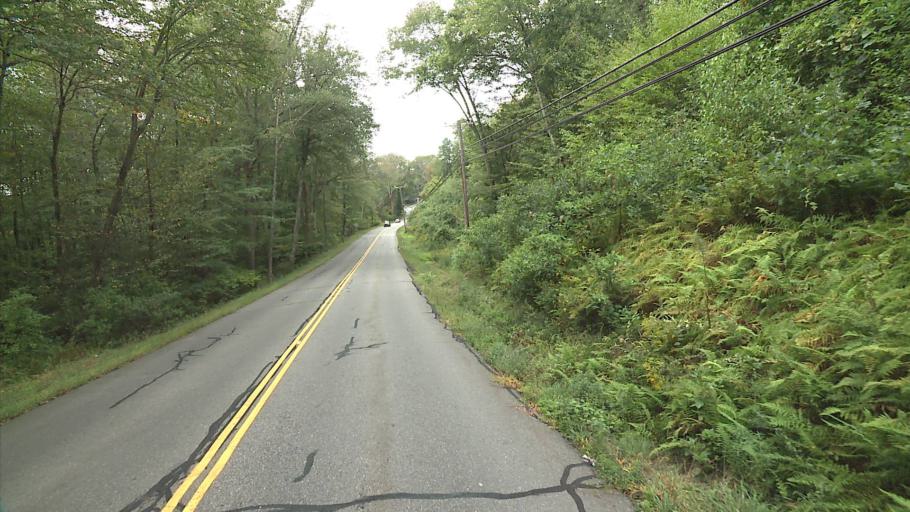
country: US
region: Connecticut
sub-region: Tolland County
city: South Coventry
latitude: 41.7735
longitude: -72.2909
